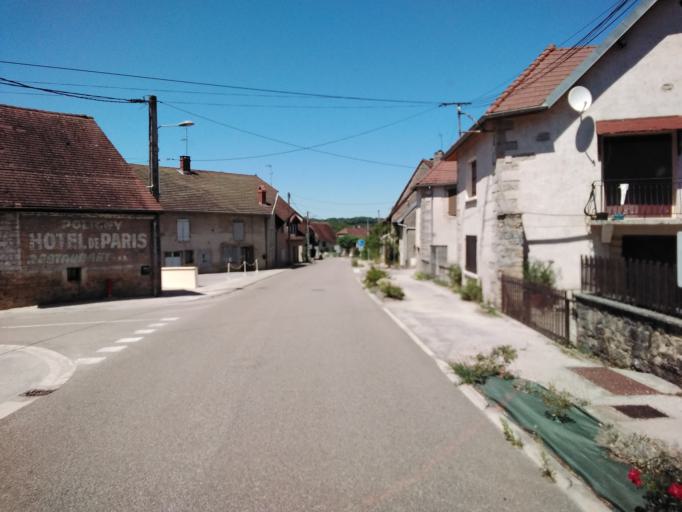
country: FR
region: Franche-Comte
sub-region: Departement du Jura
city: Montmorot
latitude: 46.7581
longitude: 5.5594
